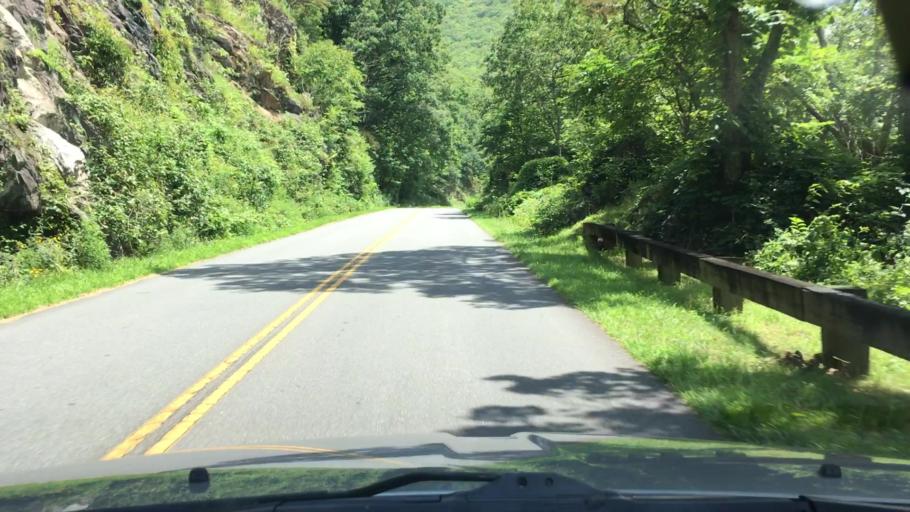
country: US
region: North Carolina
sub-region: Buncombe County
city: Swannanoa
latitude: 35.6672
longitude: -82.4644
